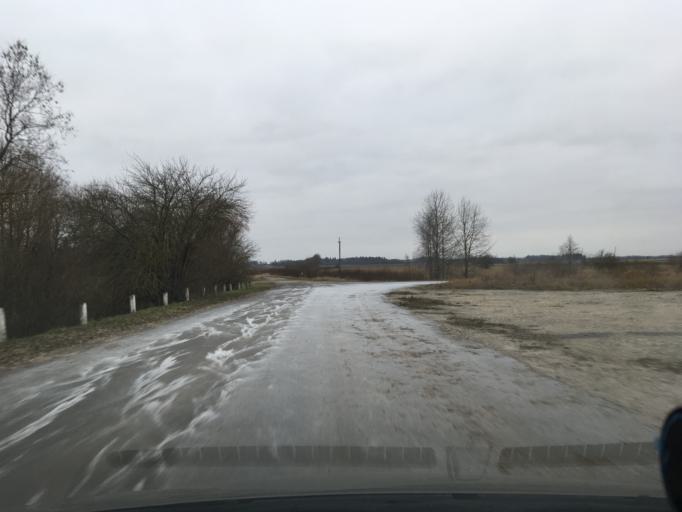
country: EE
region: Laeaene
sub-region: Lihula vald
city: Lihula
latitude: 58.7308
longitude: 23.9869
